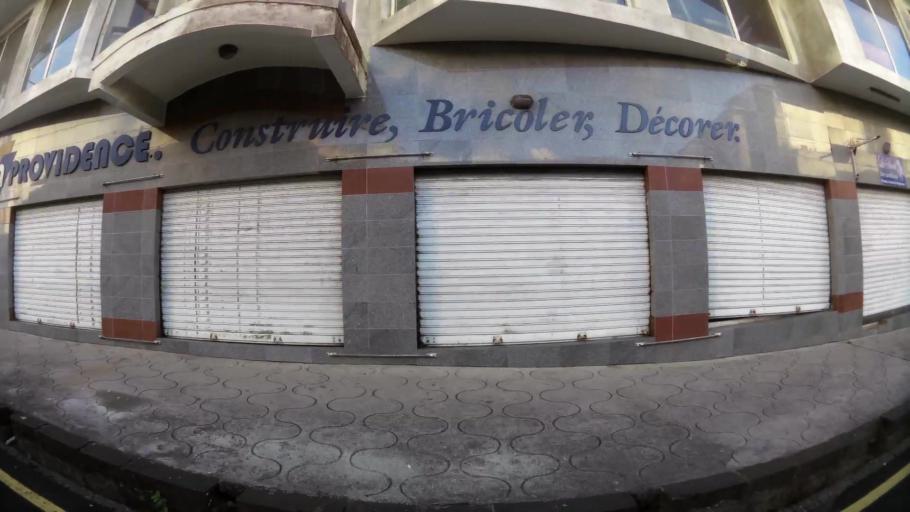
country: MU
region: Plaines Wilhems
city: Curepipe
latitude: -20.3156
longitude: 57.5231
